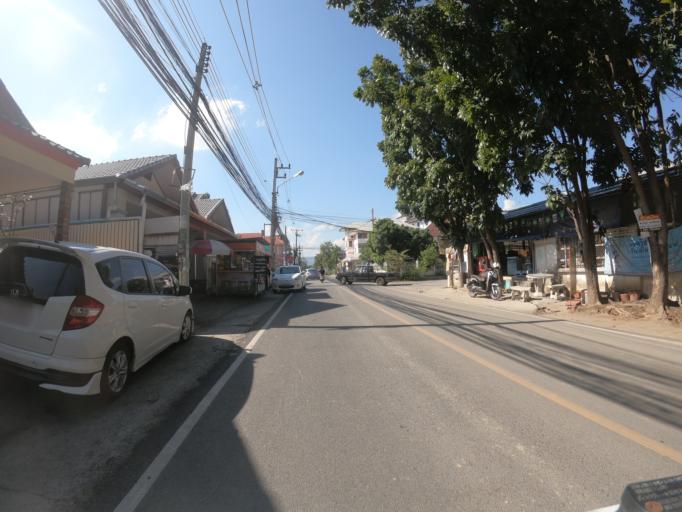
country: TH
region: Chiang Mai
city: Chiang Mai
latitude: 18.7496
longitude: 98.9780
